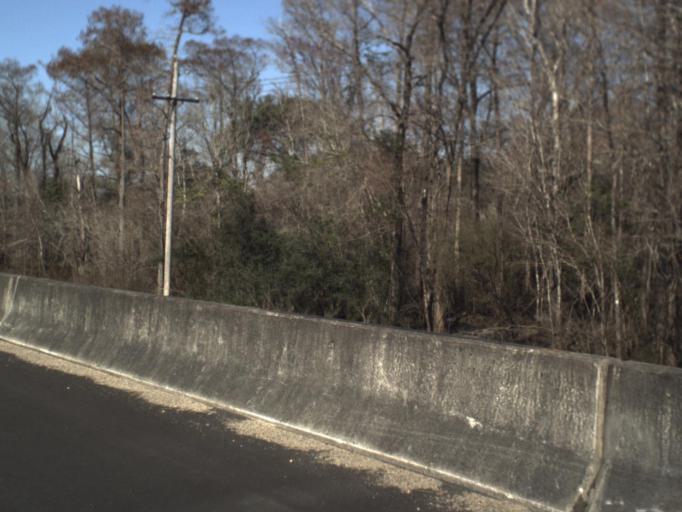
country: US
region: Florida
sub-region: Jackson County
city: Marianna
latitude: 30.6575
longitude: -85.1625
